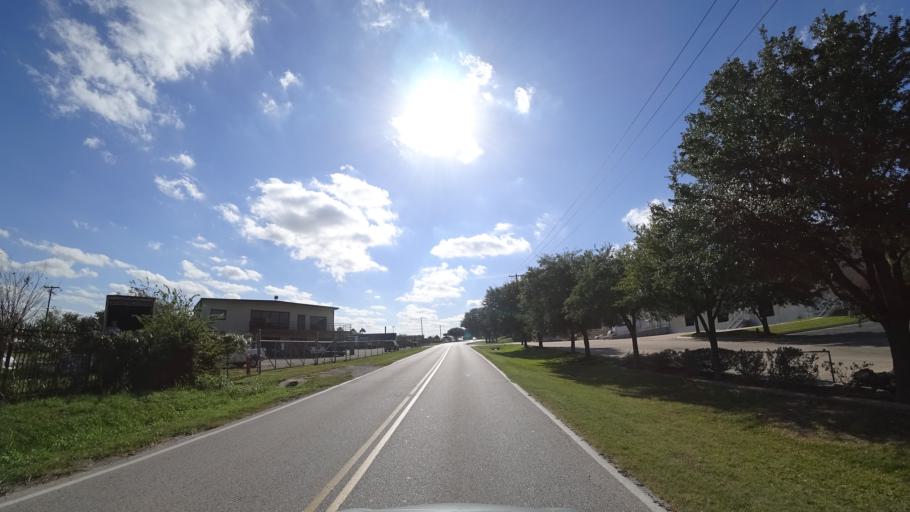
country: US
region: Texas
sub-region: Travis County
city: Wells Branch
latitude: 30.4723
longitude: -97.6733
